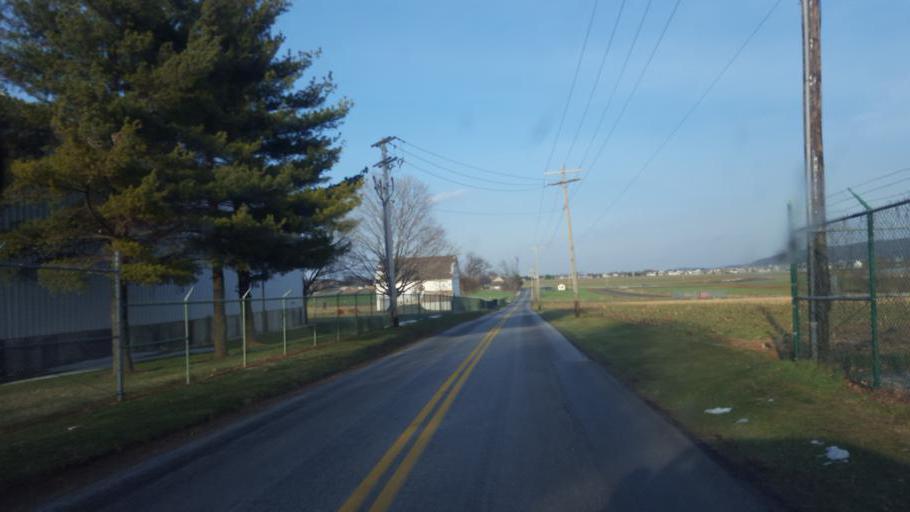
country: US
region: Pennsylvania
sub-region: Lancaster County
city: New Holland
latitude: 40.0935
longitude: -76.0849
